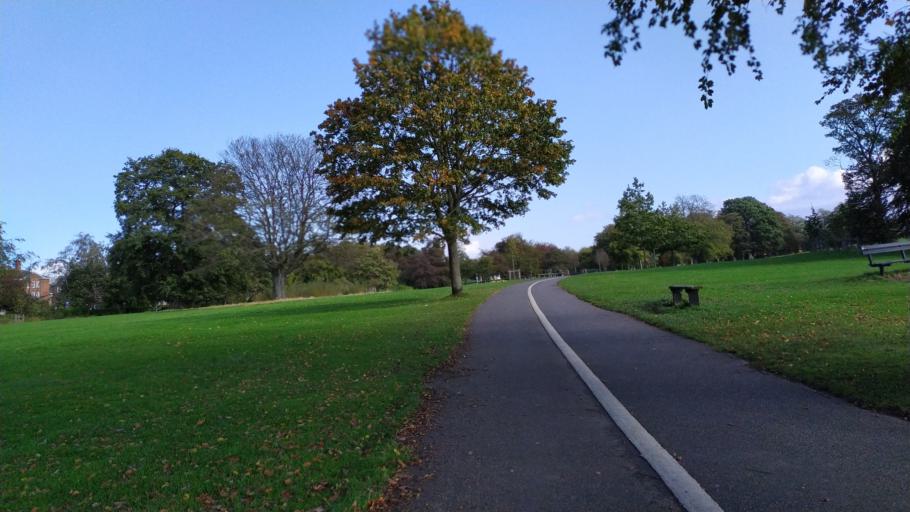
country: GB
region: England
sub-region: City and Borough of Leeds
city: Horsforth
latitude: 53.8243
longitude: -1.5933
